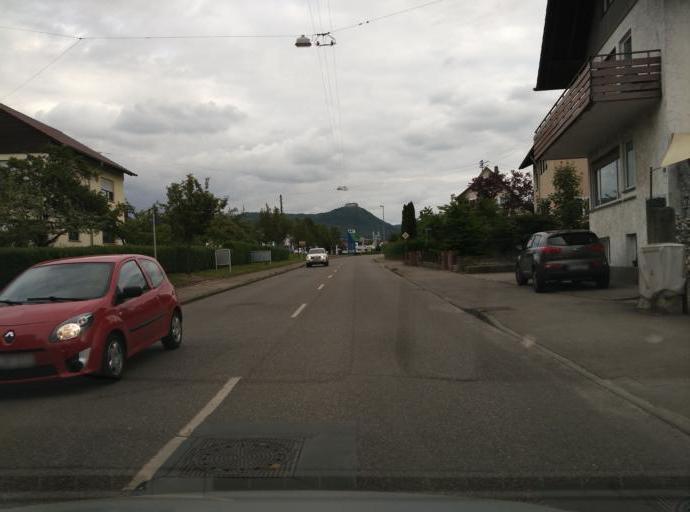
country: DE
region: Baden-Wuerttemberg
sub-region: Regierungsbezirk Stuttgart
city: Frickenhausen
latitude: 48.5878
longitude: 9.3641
